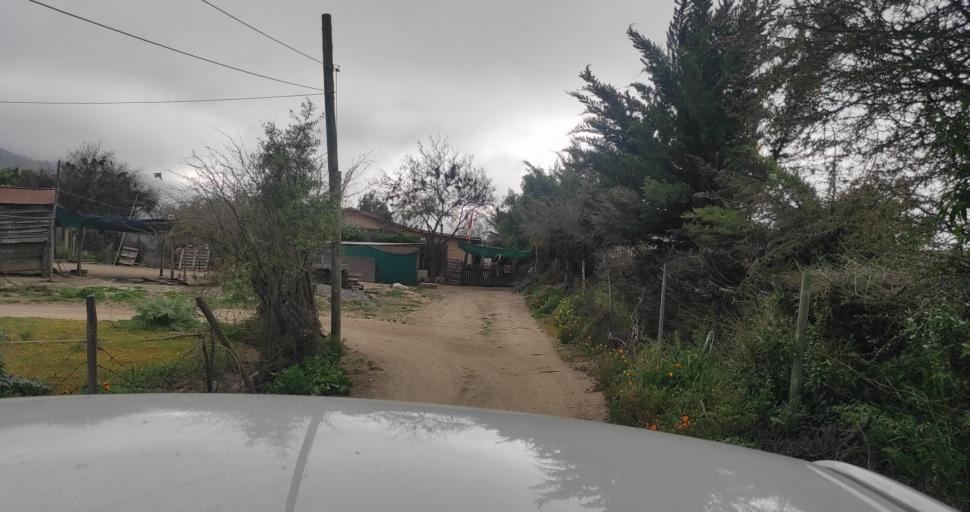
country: CL
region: Valparaiso
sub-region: Provincia de Marga Marga
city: Villa Alemana
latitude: -33.3567
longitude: -71.3019
